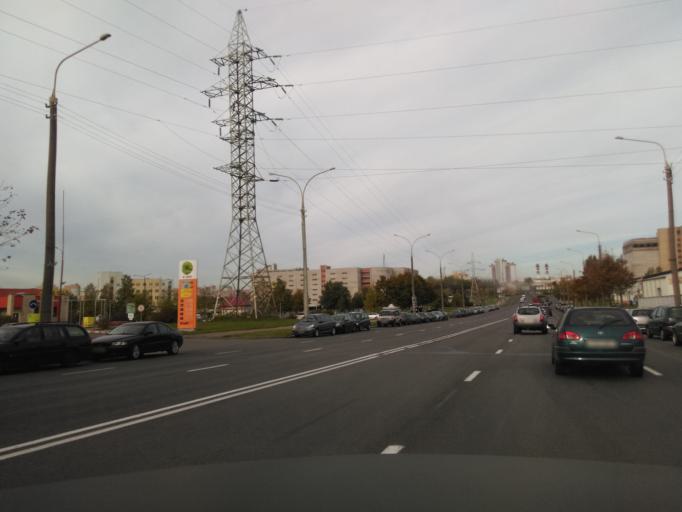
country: BY
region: Minsk
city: Minsk
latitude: 53.8793
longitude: 27.5879
